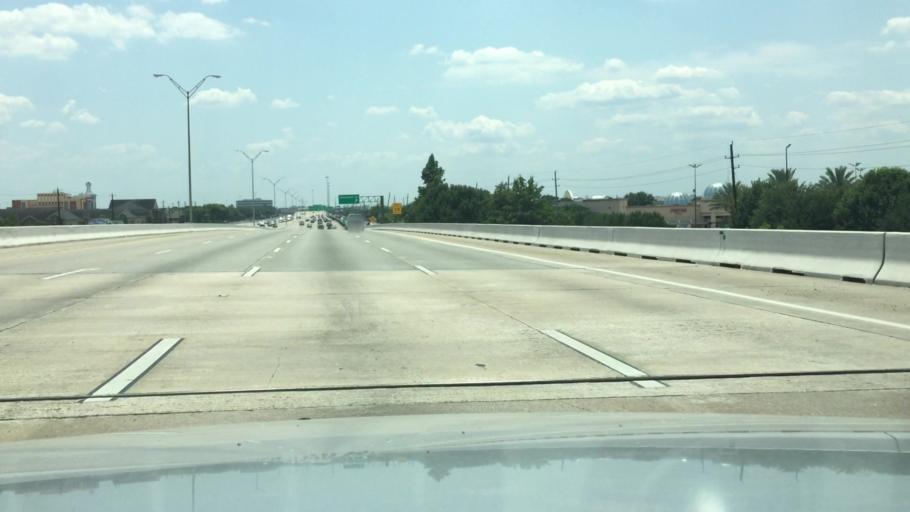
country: US
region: Texas
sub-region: Fort Bend County
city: Meadows Place
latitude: 29.6890
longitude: -95.5576
